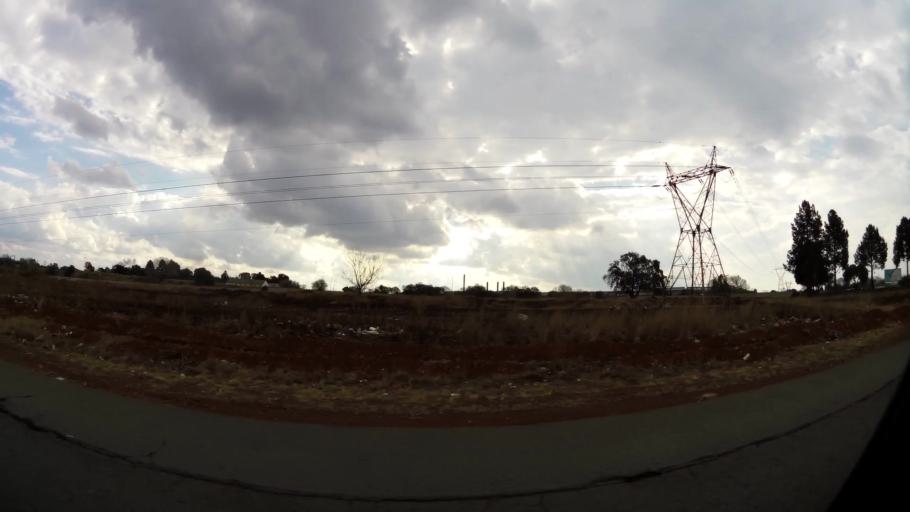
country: ZA
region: Gauteng
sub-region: Sedibeng District Municipality
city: Vanderbijlpark
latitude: -26.6616
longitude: 27.8441
